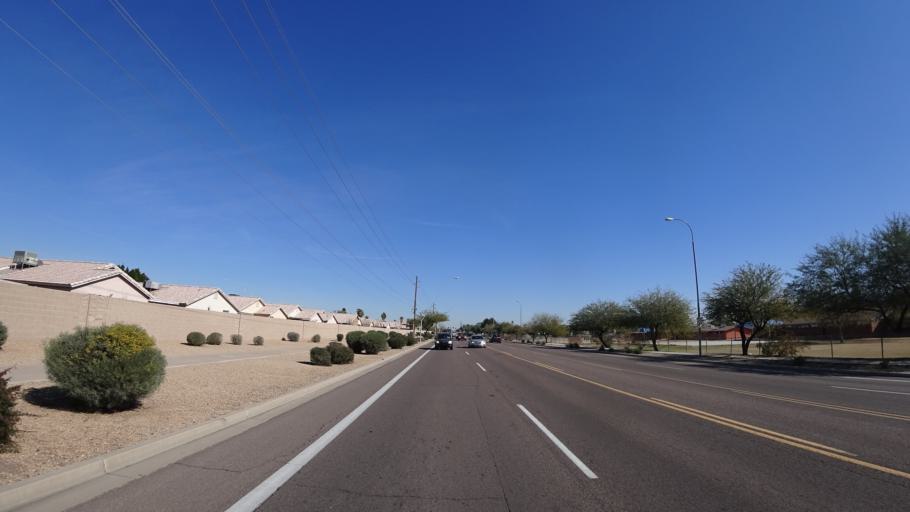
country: US
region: Arizona
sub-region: Maricopa County
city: Tolleson
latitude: 33.5083
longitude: -112.2849
